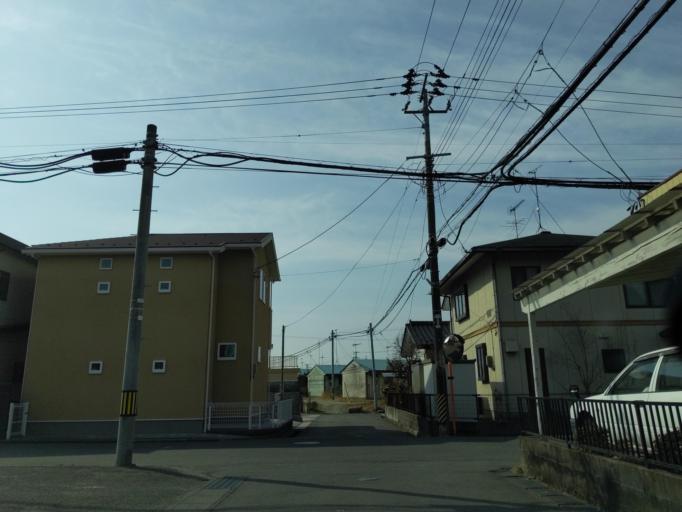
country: JP
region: Fukushima
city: Koriyama
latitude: 37.4247
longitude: 140.3535
